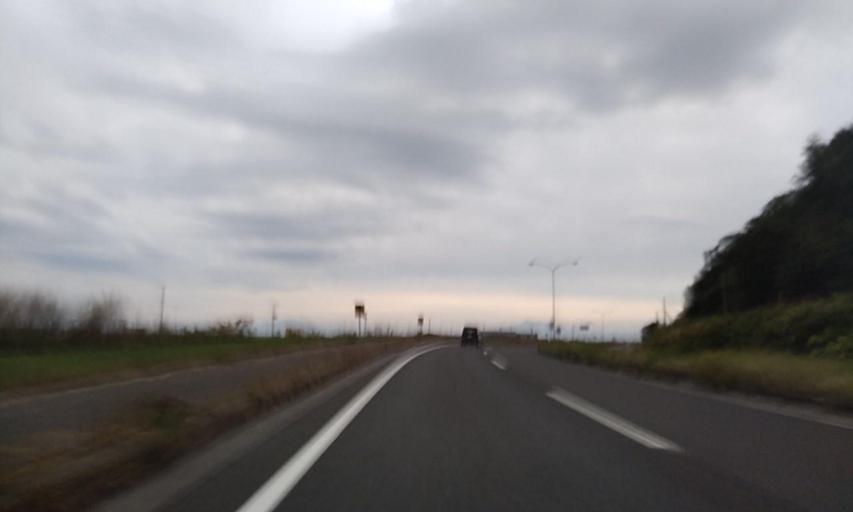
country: JP
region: Hokkaido
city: Abashiri
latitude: 44.0087
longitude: 144.2825
